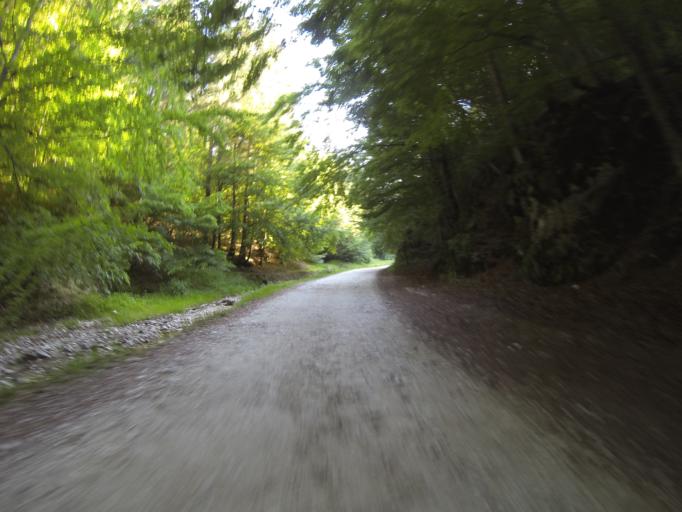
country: RO
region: Brasov
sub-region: Comuna Zarnesti
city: Zarnesti
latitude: 45.5298
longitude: 25.2873
